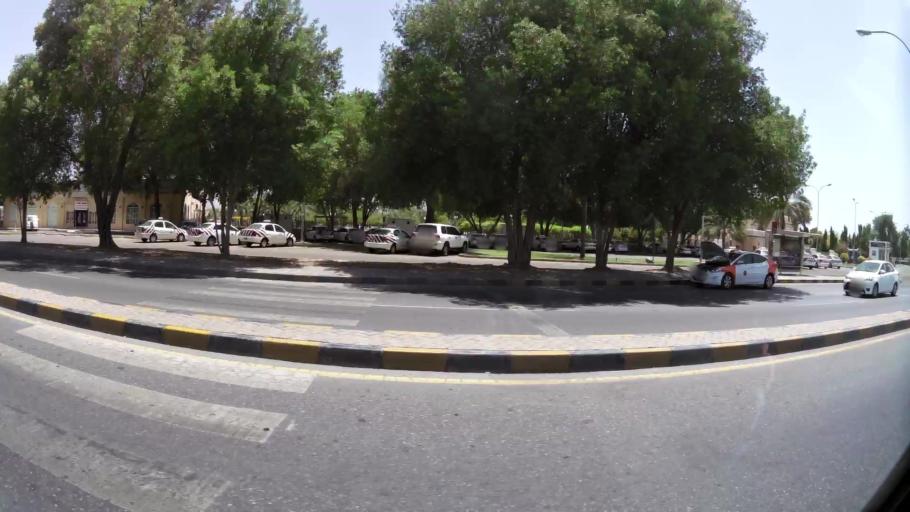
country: OM
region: Muhafazat Masqat
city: Muscat
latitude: 23.6217
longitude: 58.4935
